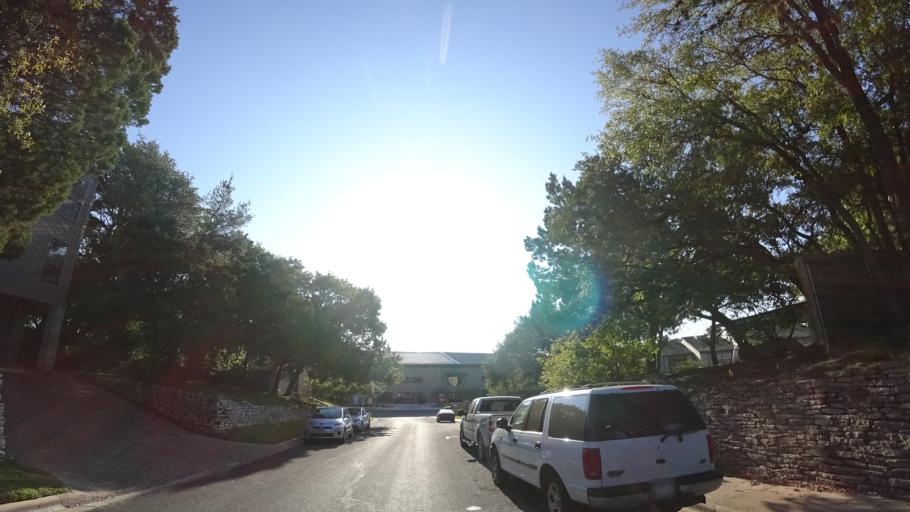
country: US
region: Texas
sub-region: Travis County
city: Rollingwood
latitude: 30.2604
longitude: -97.7990
